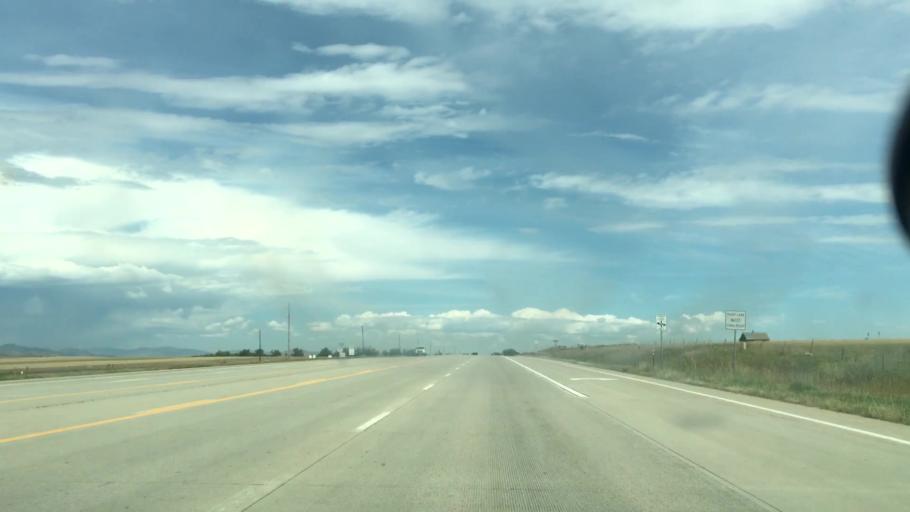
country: US
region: Colorado
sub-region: Boulder County
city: Longmont
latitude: 40.2159
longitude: -105.1023
